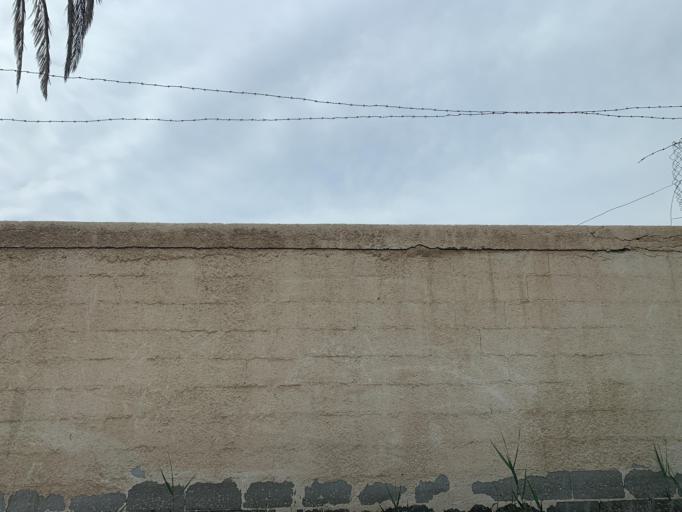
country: BH
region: Central Governorate
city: Madinat Hamad
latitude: 26.1121
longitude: 50.4701
